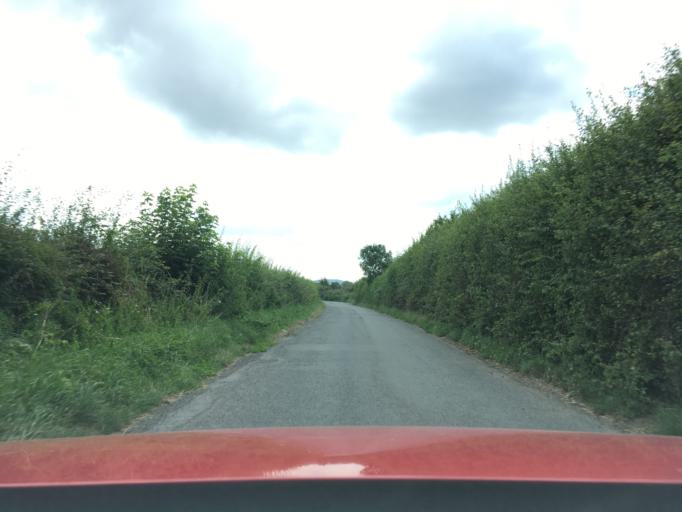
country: GB
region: England
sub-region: Gloucestershire
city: Gloucester
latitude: 51.9044
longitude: -2.2231
